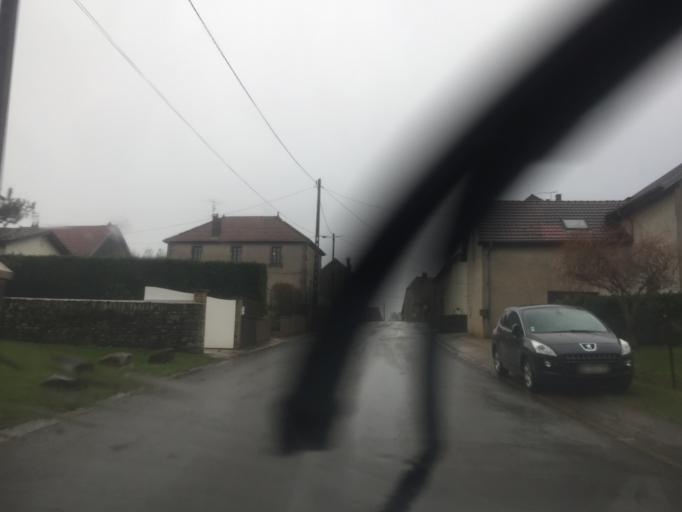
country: FR
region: Franche-Comte
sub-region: Departement du Jura
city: Dampierre
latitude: 47.2177
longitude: 5.7368
